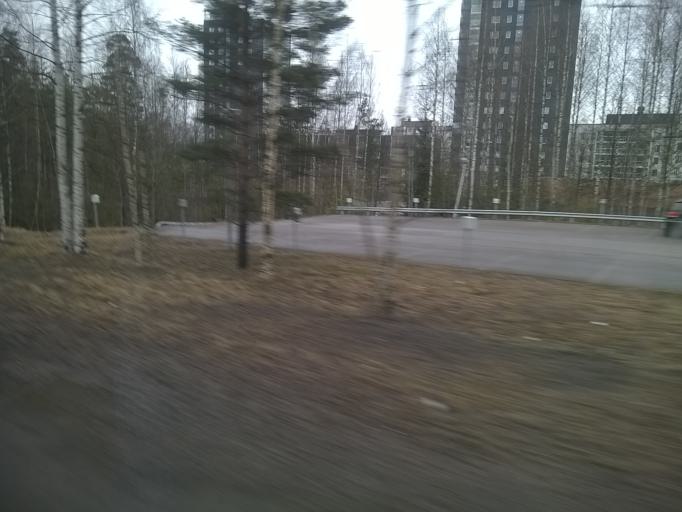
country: FI
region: Pirkanmaa
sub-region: Tampere
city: Tampere
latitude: 61.4562
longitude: 23.8461
